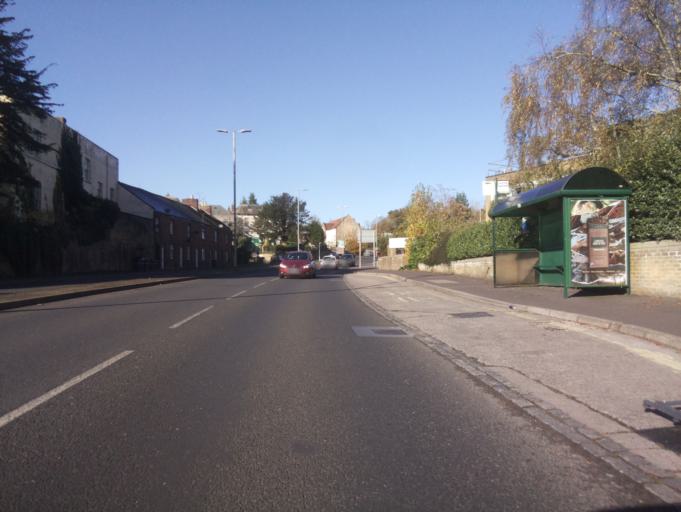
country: GB
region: England
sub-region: Somerset
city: Yeovil
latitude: 50.9447
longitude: -2.6357
